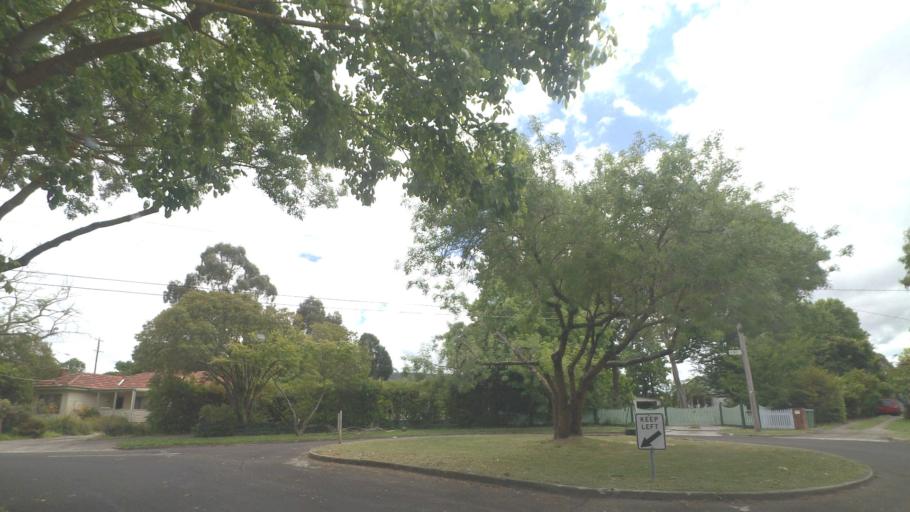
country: AU
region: Victoria
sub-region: Yarra Ranges
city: Kilsyth
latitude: -37.8001
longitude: 145.3057
